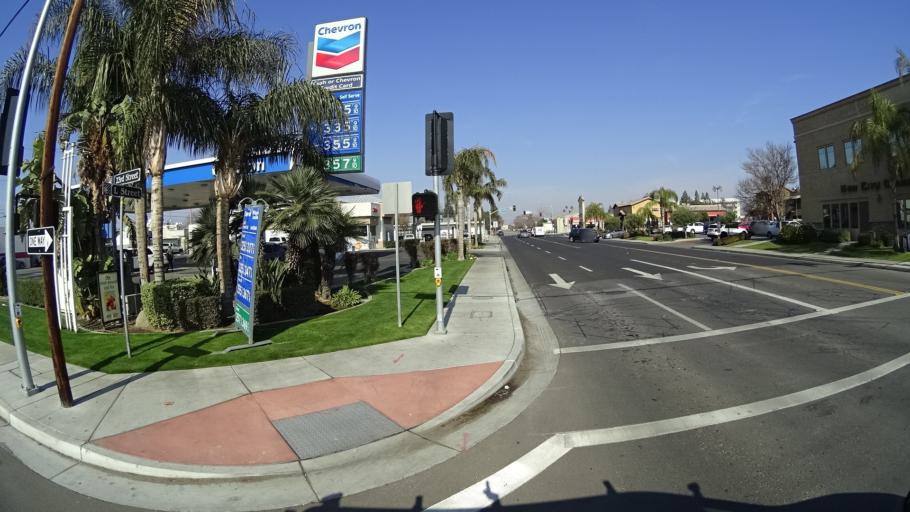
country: US
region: California
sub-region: Kern County
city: Bakersfield
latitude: 35.3801
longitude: -119.0166
